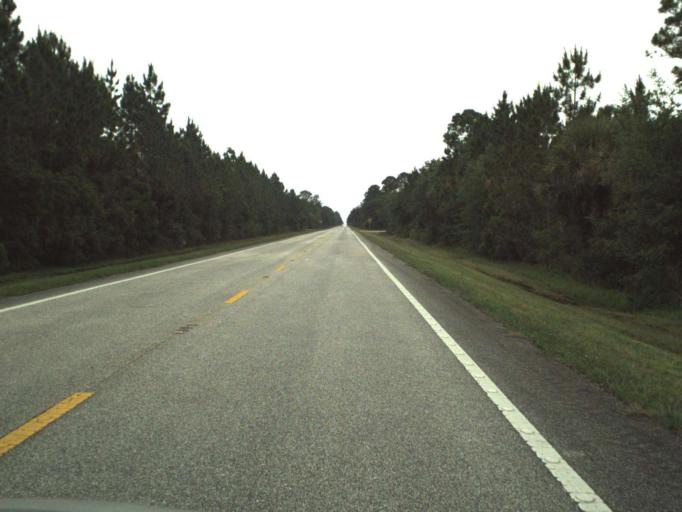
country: US
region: Florida
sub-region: Brevard County
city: Mims
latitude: 28.6705
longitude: -80.9703
